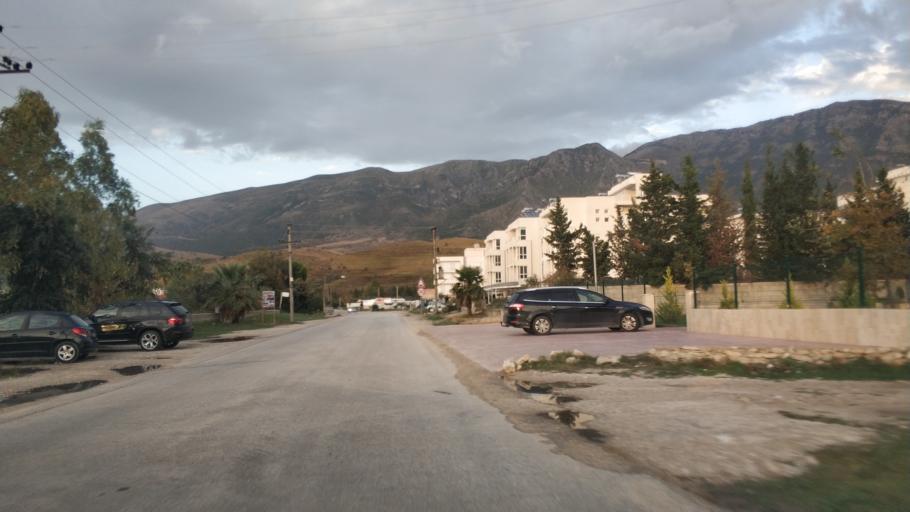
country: AL
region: Vlore
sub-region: Rrethi i Vlores
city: Orikum
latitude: 40.3434
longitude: 19.4818
